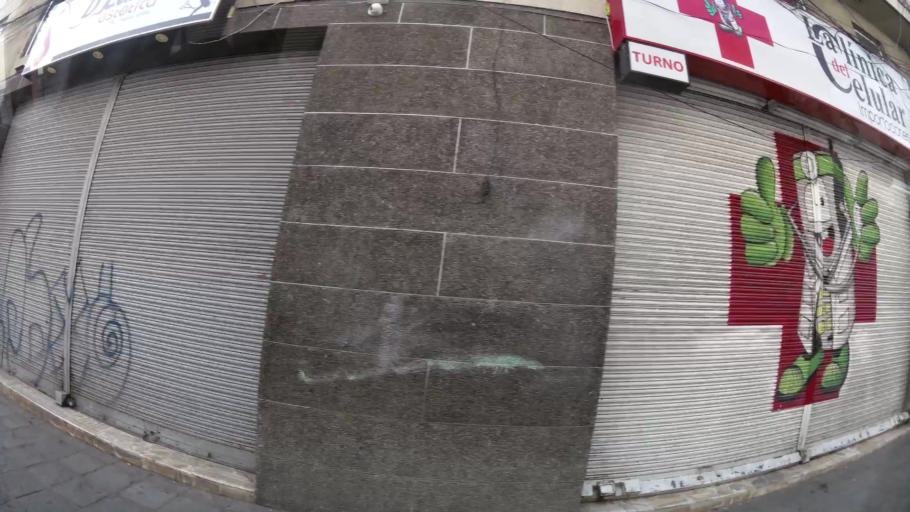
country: EC
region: Cotopaxi
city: Latacunga
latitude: -0.9330
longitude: -78.6165
